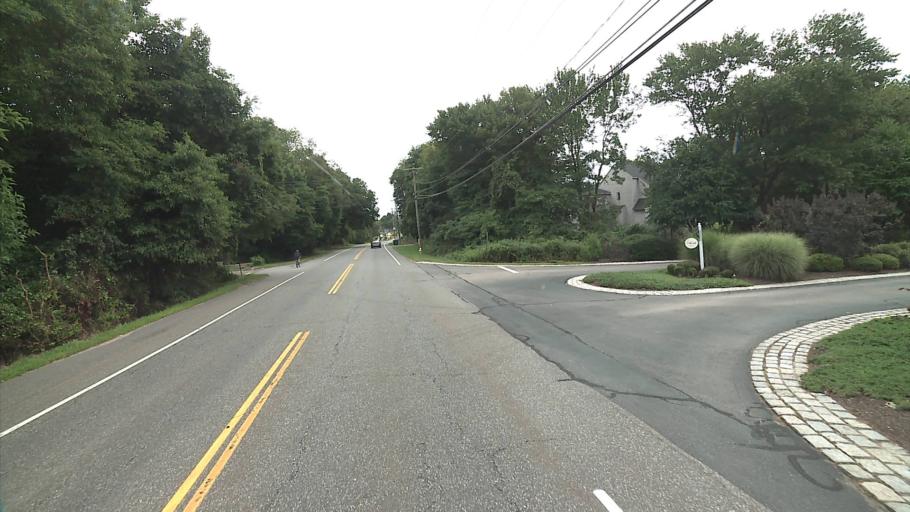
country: US
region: Connecticut
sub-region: Middlesex County
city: Old Saybrook Center
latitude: 41.2876
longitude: -72.2943
